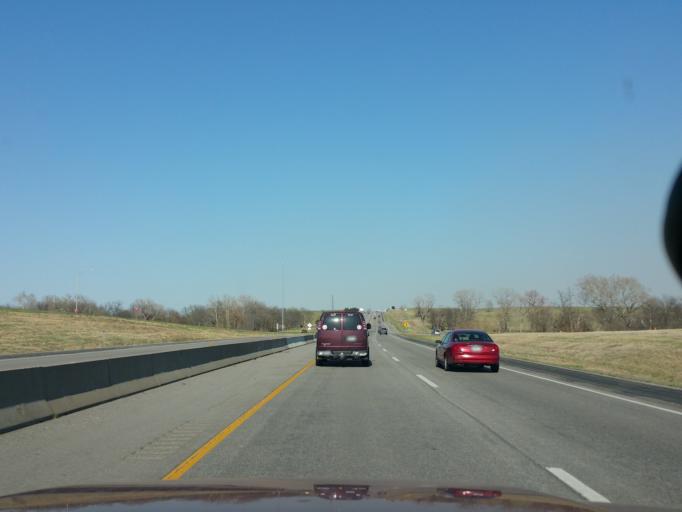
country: US
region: Kansas
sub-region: Leavenworth County
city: Tonganoxie
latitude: 39.0445
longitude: -95.0921
